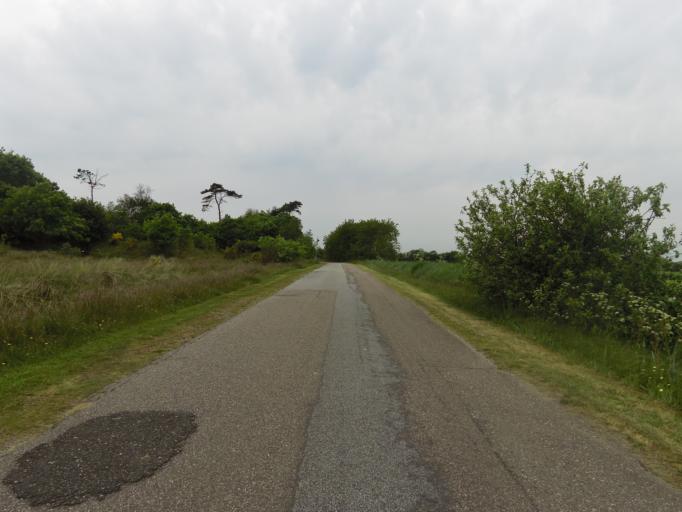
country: DK
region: South Denmark
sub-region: Esbjerg Kommune
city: Ribe
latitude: 55.3248
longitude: 8.8191
